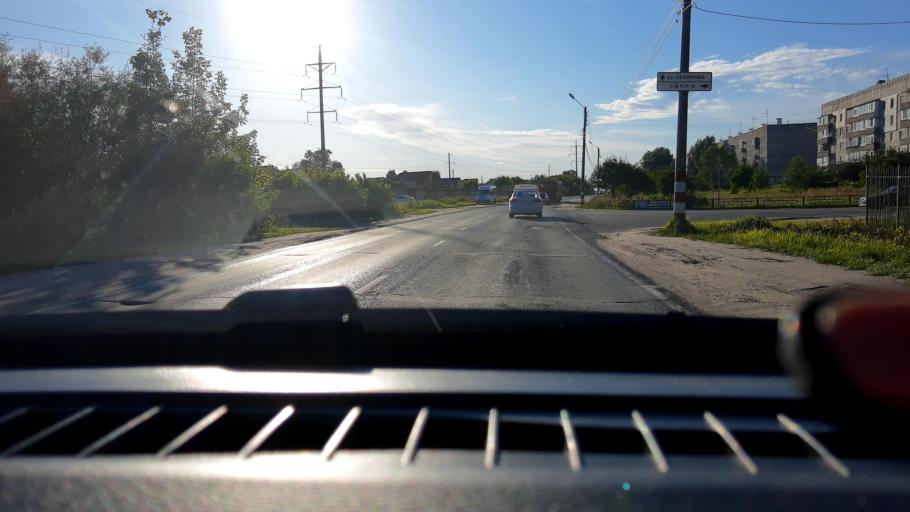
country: RU
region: Nizjnij Novgorod
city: Bor
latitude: 56.3366
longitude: 44.1266
